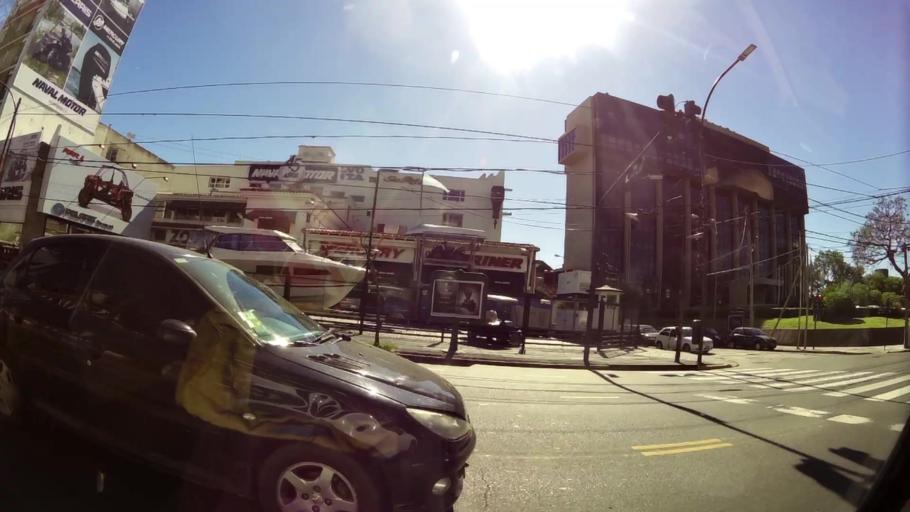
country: AR
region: Buenos Aires
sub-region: Partido de Vicente Lopez
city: Olivos
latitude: -34.5274
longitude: -58.4710
